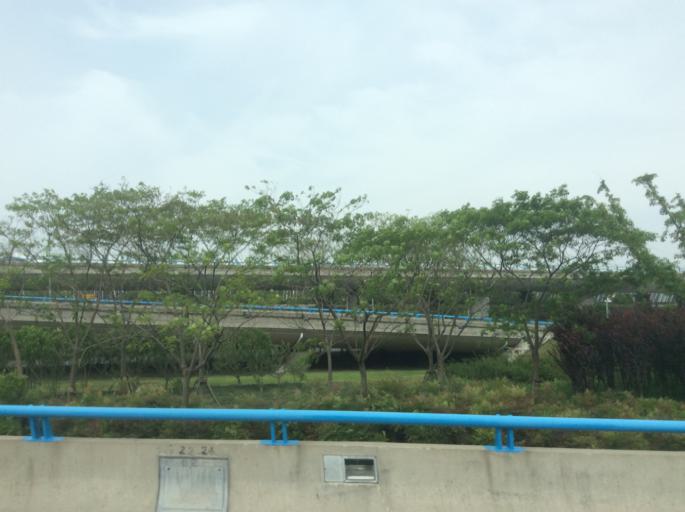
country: CN
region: Shanghai Shi
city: Laogang
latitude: 31.1469
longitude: 121.8024
